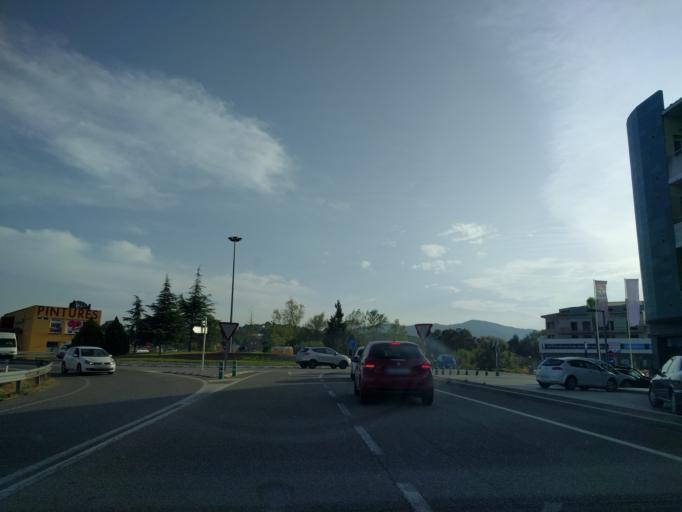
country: ES
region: Catalonia
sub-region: Provincia de Barcelona
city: Tordera
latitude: 41.6933
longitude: 2.7236
